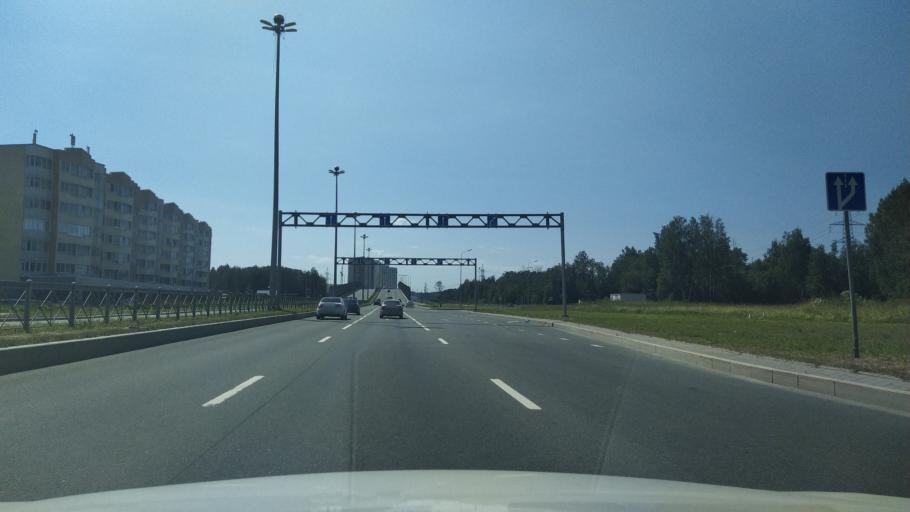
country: RU
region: St.-Petersburg
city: Shuvalovo
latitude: 60.0643
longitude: 30.2916
